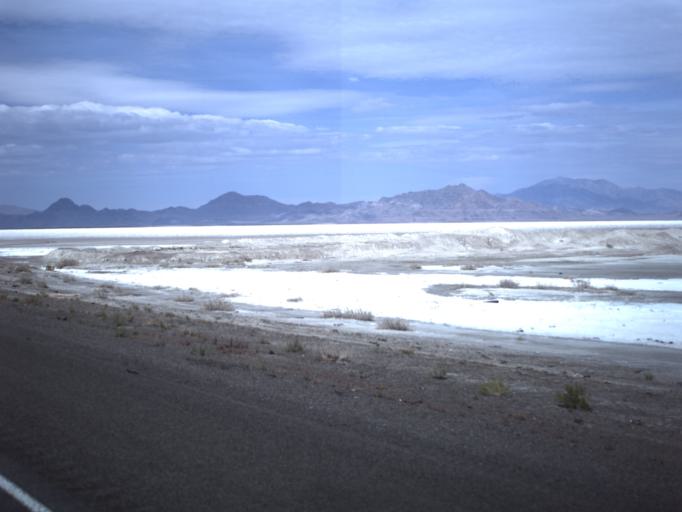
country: US
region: Utah
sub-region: Tooele County
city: Wendover
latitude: 40.7381
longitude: -113.7882
